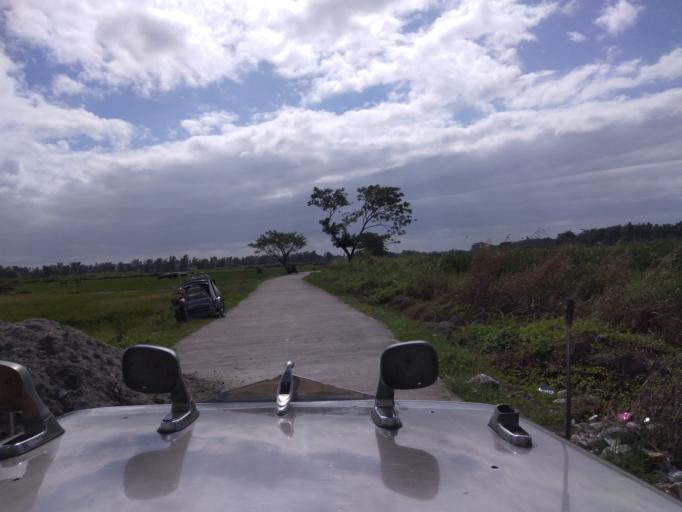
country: PH
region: Central Luzon
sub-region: Province of Pampanga
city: San Patricio
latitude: 15.0878
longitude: 120.7174
